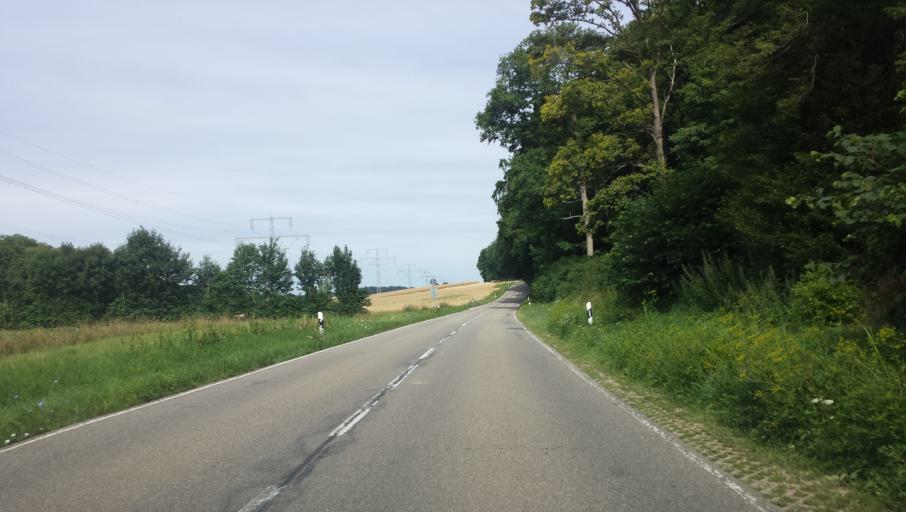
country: DE
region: Baden-Wuerttemberg
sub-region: Karlsruhe Region
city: Waibstadt
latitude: 49.2827
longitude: 8.8933
